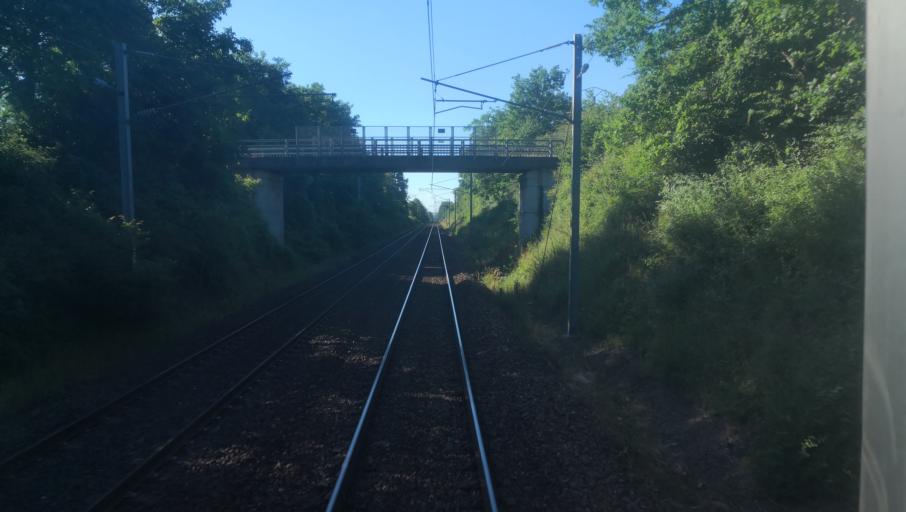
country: FR
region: Centre
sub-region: Departement du Cher
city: Herry
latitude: 47.2496
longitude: 3.0022
